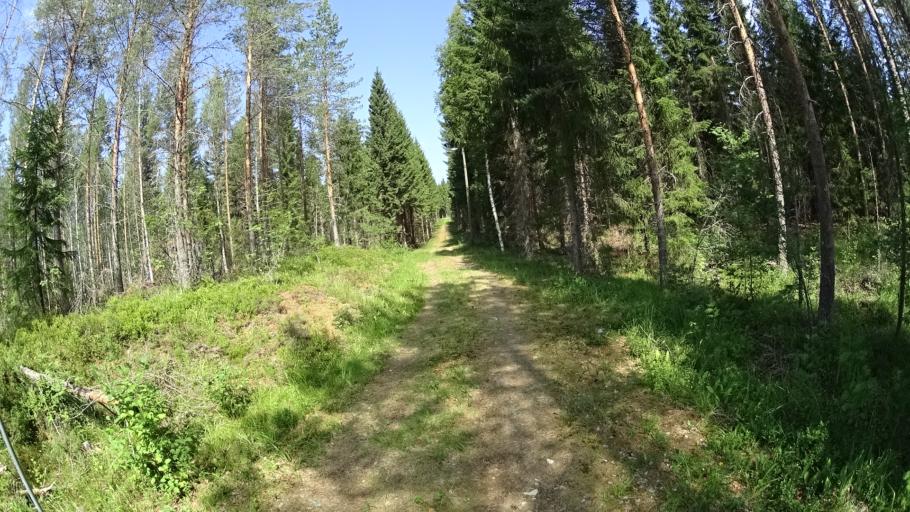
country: FI
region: North Karelia
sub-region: Pielisen Karjala
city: Lieksa
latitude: 63.1258
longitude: 29.7997
